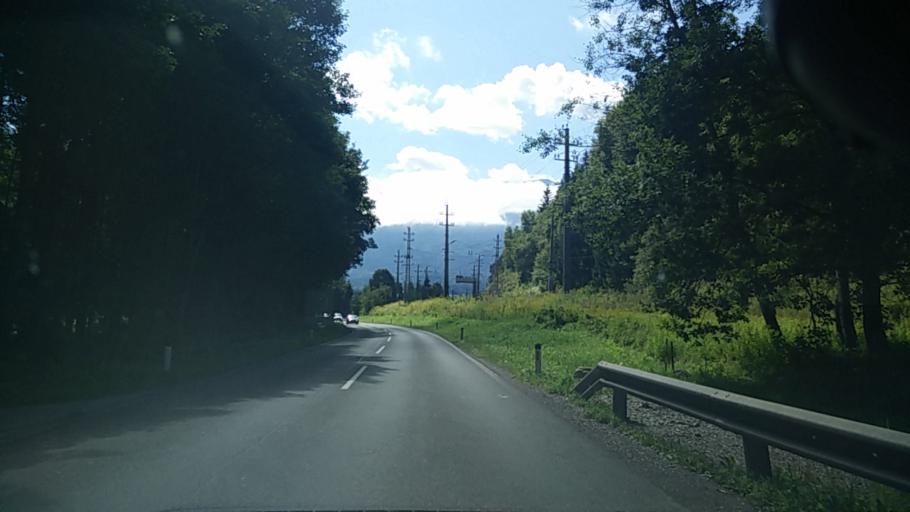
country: AT
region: Carinthia
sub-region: Politischer Bezirk Villach Land
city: Finkenstein am Faaker See
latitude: 46.5752
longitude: 13.8374
